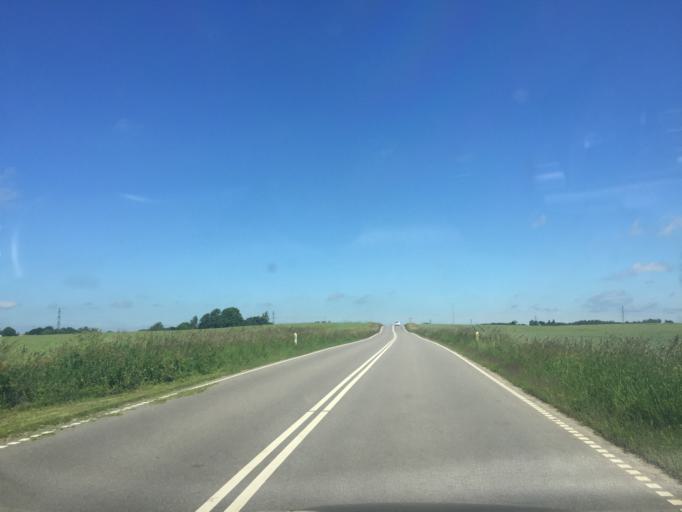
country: DK
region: Capital Region
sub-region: Hoje-Taastrup Kommune
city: Flong
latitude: 55.6697
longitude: 12.2100
